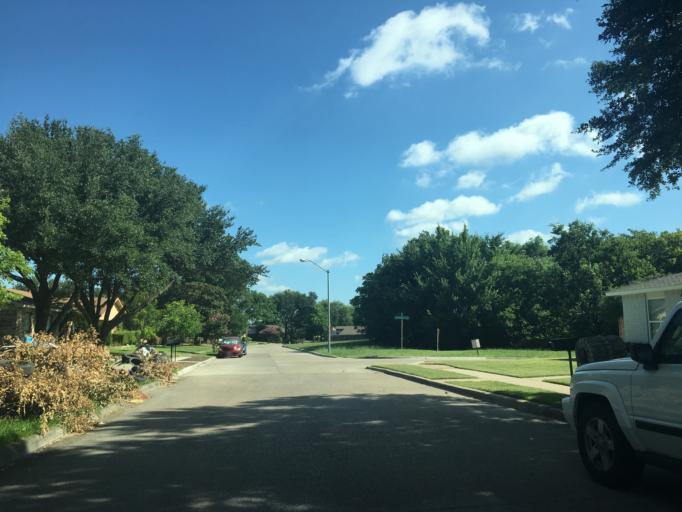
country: US
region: Texas
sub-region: Dallas County
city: Garland
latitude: 32.8512
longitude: -96.6591
